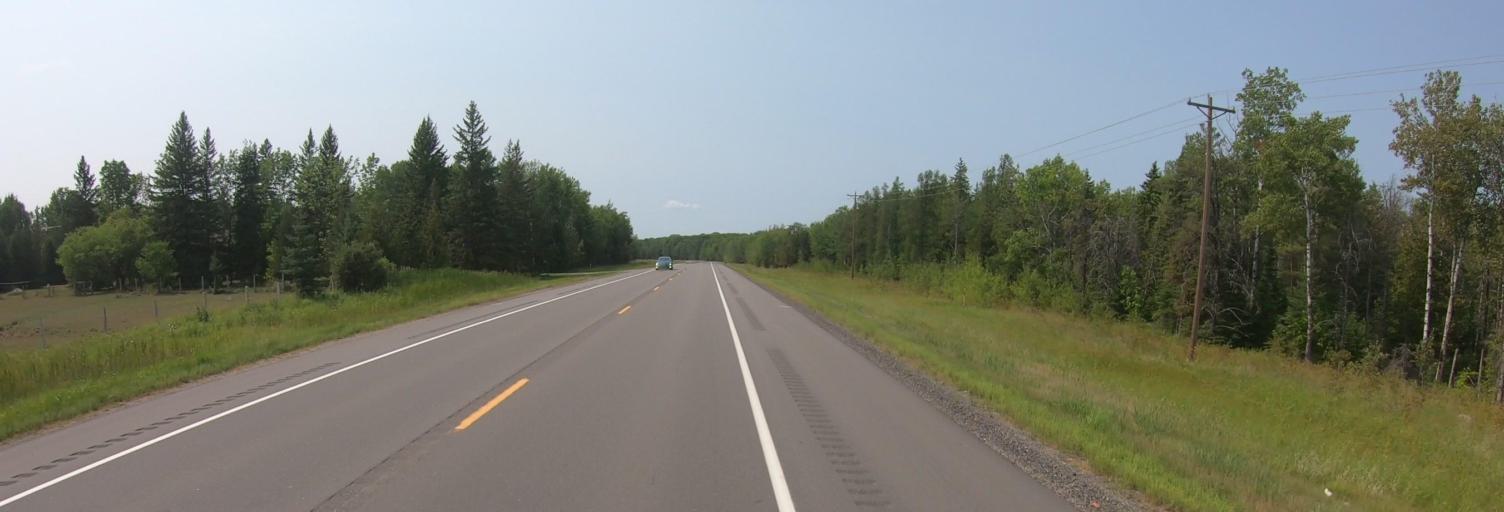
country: US
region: Minnesota
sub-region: Koochiching County
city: International Falls
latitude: 48.5309
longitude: -93.5189
